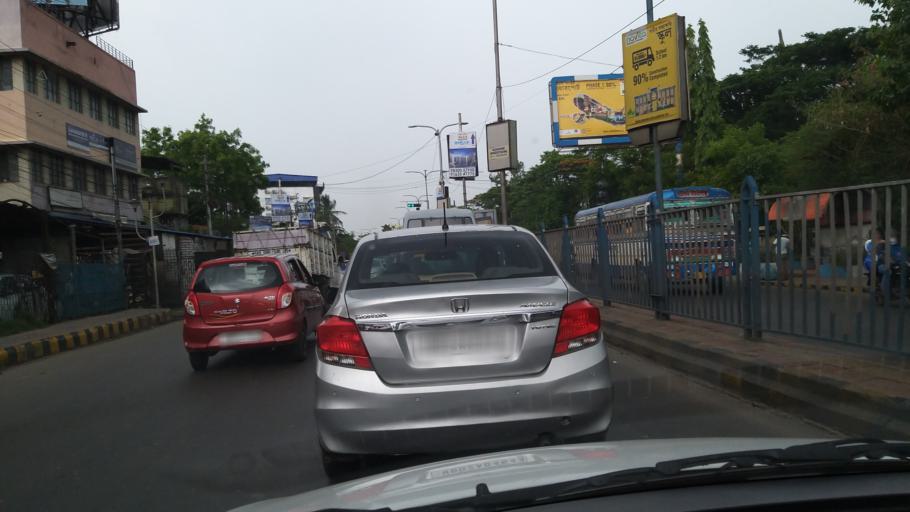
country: IN
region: West Bengal
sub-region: North 24 Parganas
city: Dam Dam
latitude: 22.6554
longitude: 88.4398
